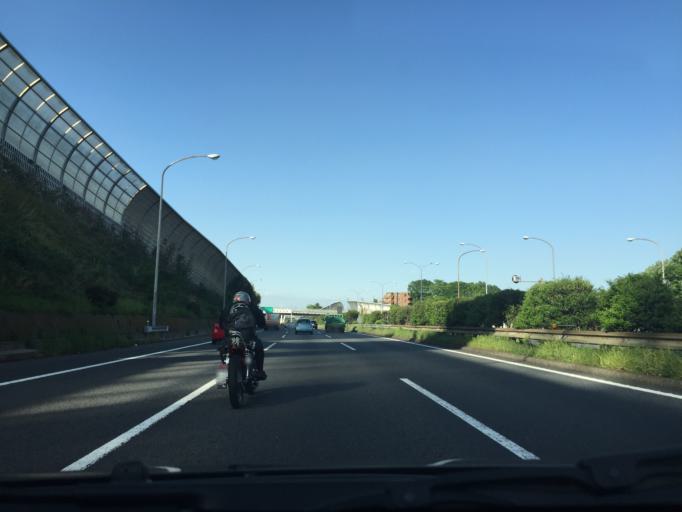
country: JP
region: Tokyo
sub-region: Machida-shi
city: Machida
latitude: 35.5348
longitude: 139.5314
